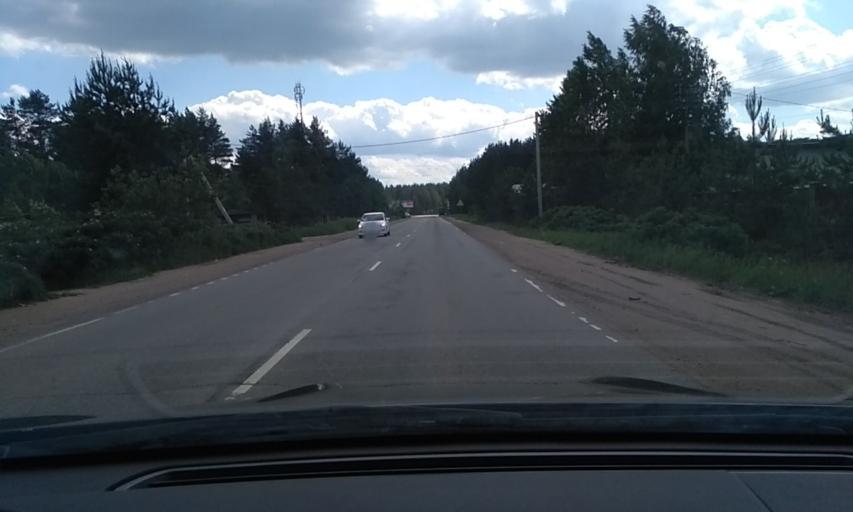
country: RU
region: Leningrad
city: Imeni Sverdlova
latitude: 59.8624
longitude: 30.6713
